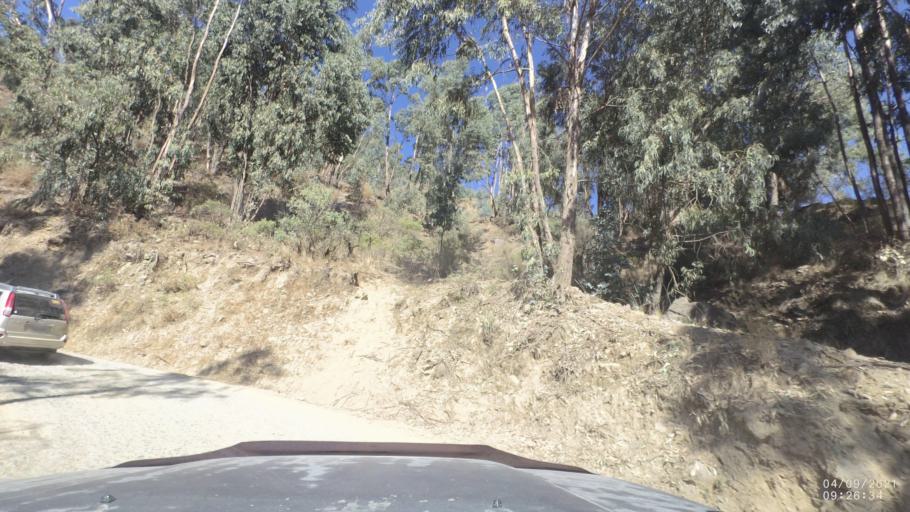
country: BO
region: Cochabamba
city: Sipe Sipe
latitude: -17.3573
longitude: -66.3716
